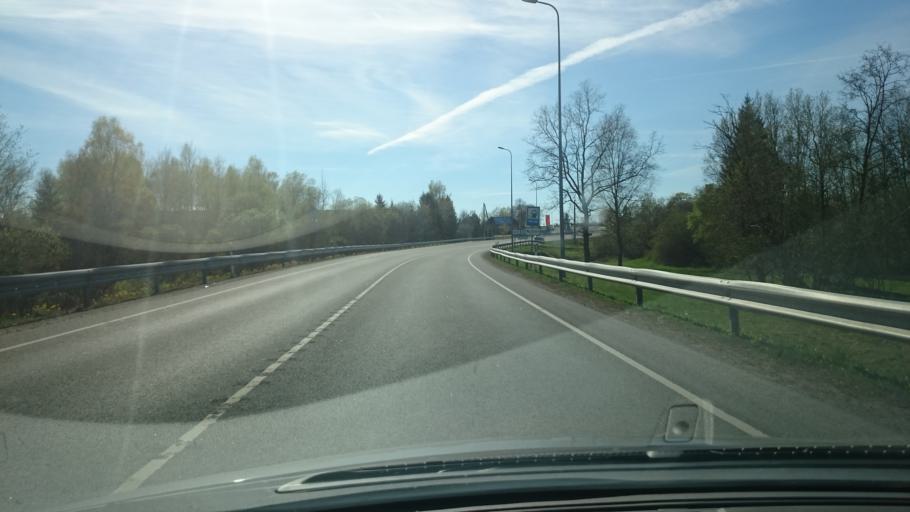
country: EE
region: Laeaene-Virumaa
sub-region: Someru vald
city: Someru
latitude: 59.3649
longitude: 26.4388
